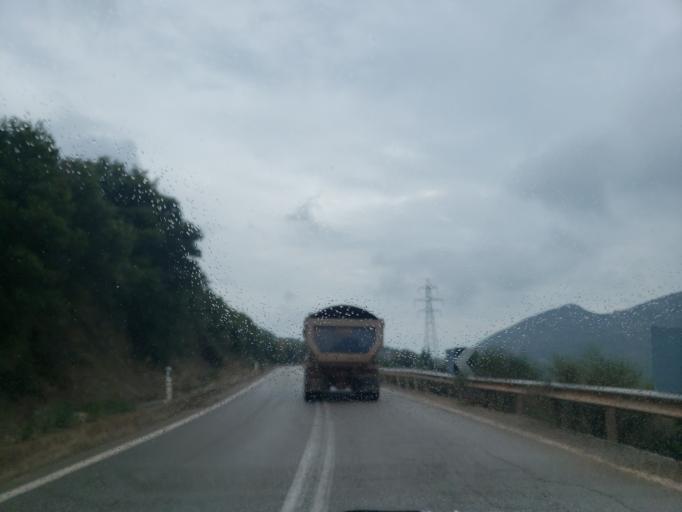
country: GR
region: Central Greece
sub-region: Nomos Fokidos
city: Amfissa
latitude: 38.5790
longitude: 22.3930
